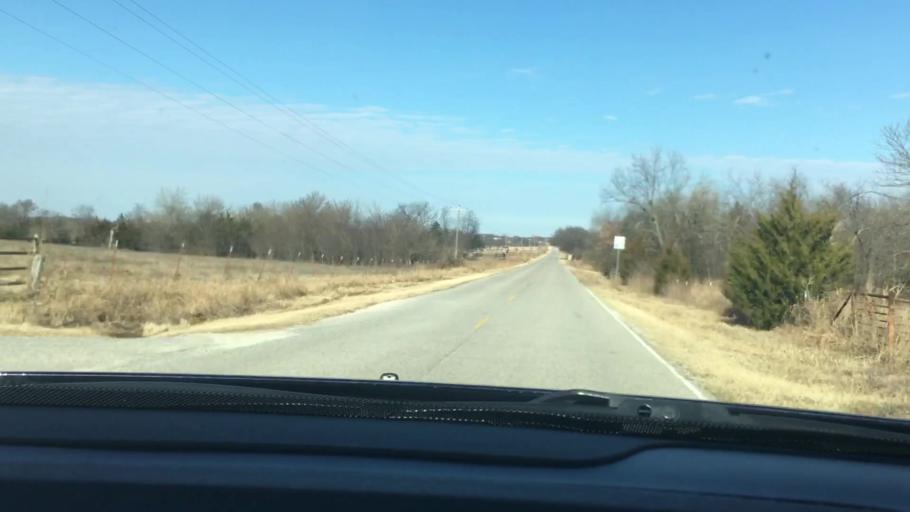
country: US
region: Oklahoma
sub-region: Garvin County
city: Wynnewood
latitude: 34.7095
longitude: -97.1254
